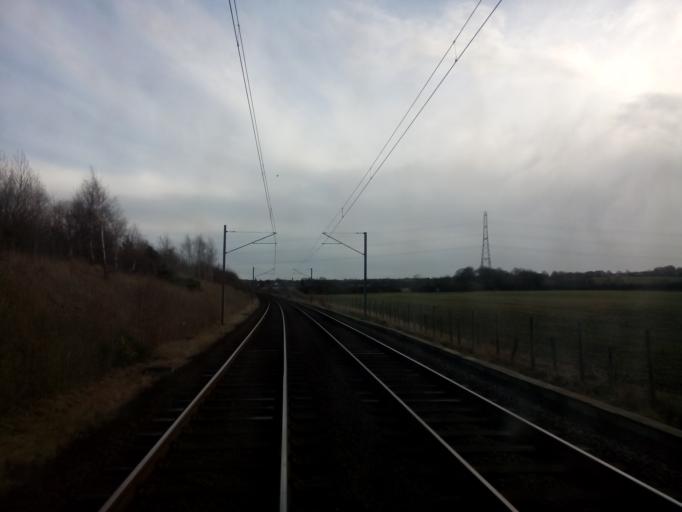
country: GB
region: England
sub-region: Newcastle upon Tyne
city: Dinnington
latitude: 55.0191
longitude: -1.6924
